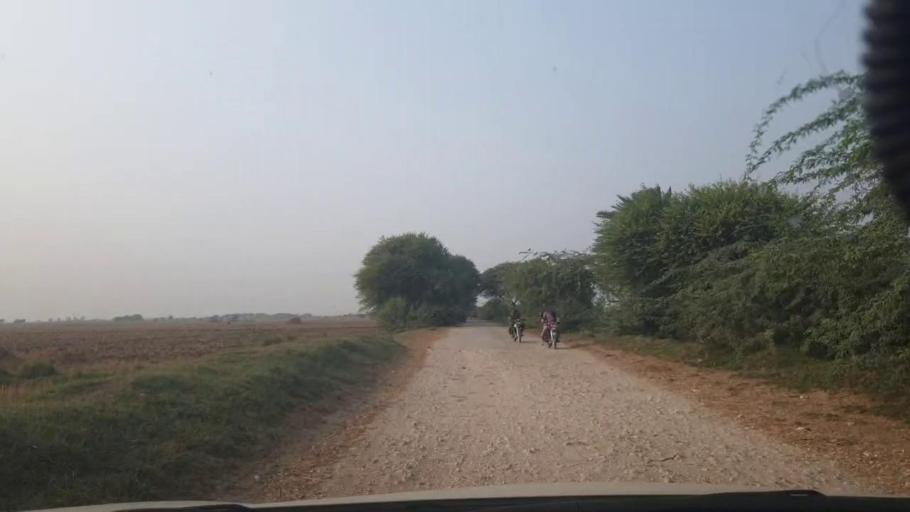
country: PK
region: Sindh
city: Bulri
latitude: 24.8058
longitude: 68.4108
